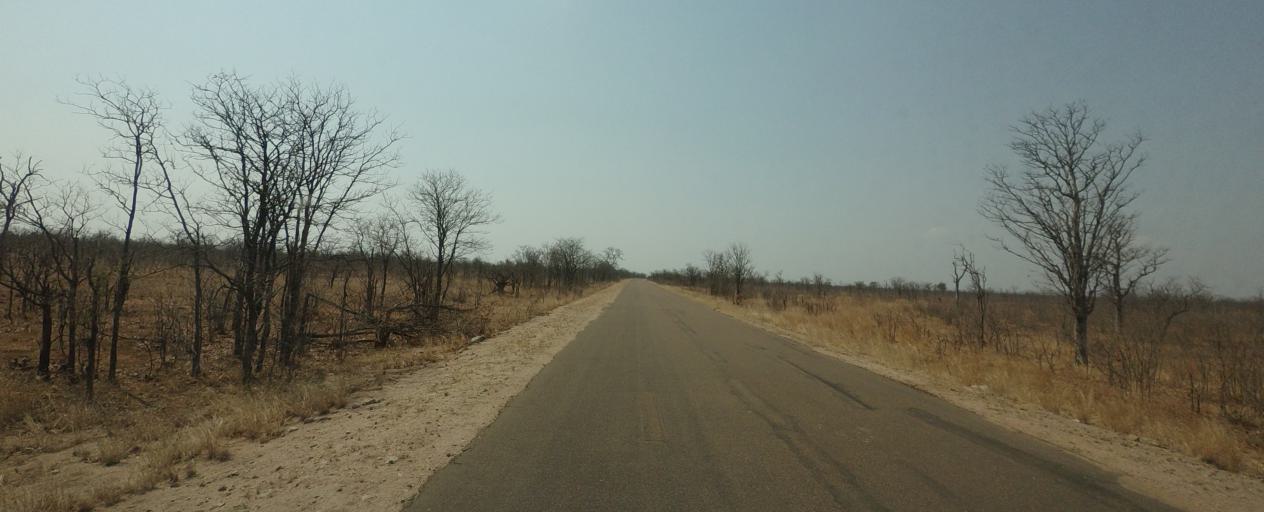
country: ZA
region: Limpopo
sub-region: Mopani District Municipality
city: Giyani
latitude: -23.3569
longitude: 31.3190
